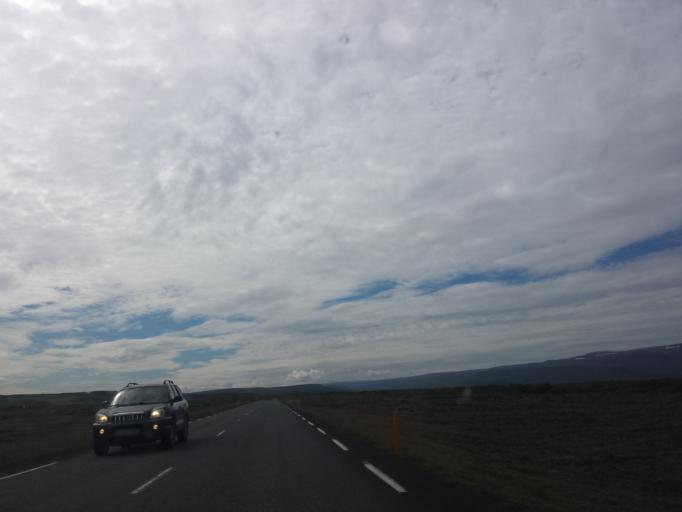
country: IS
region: Northeast
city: Husavik
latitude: 65.9593
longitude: -17.4263
